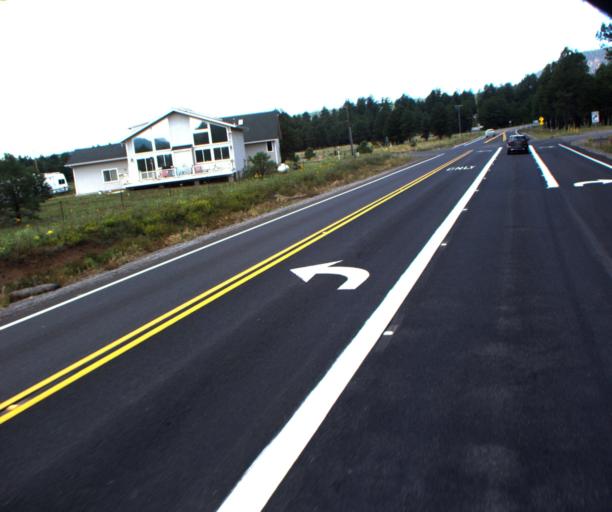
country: US
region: Arizona
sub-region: Coconino County
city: Flagstaff
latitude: 35.2680
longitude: -111.7358
